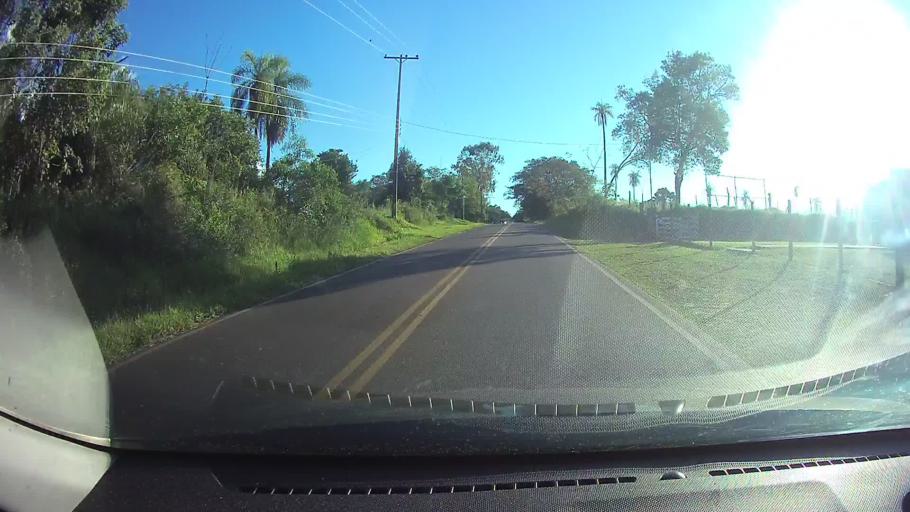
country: PY
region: Cordillera
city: Emboscada
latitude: -25.1992
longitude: -57.3209
